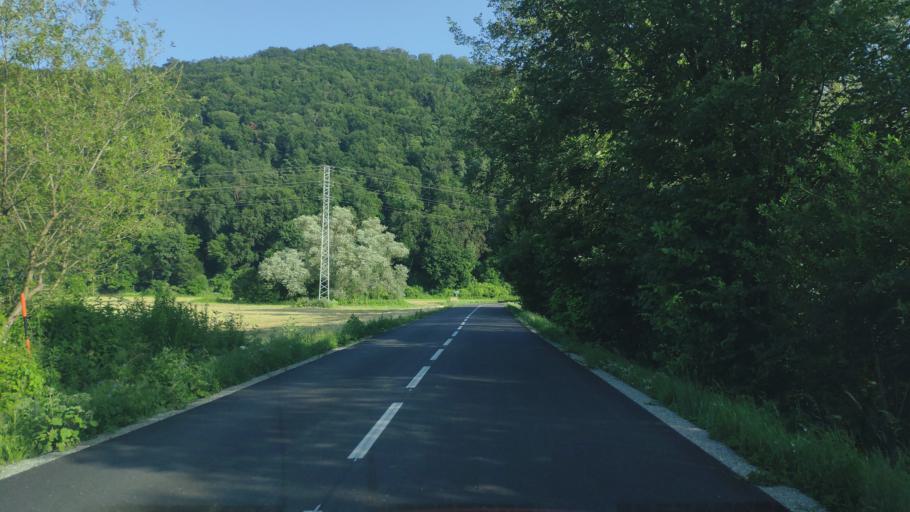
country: SK
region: Kosicky
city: Kosice
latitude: 48.8457
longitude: 21.2279
